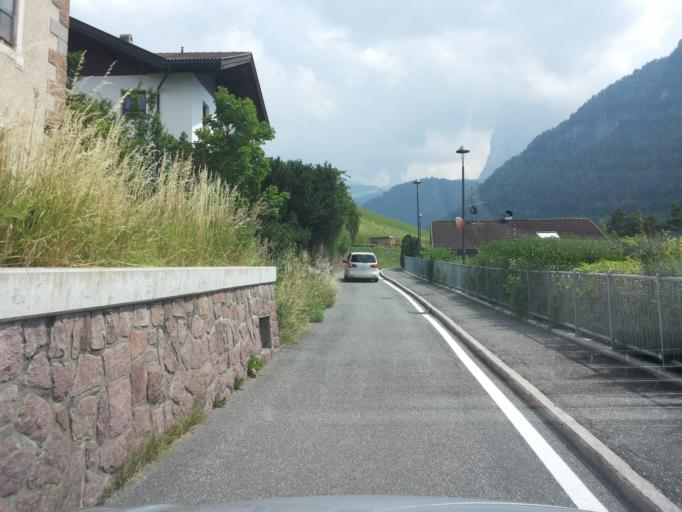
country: IT
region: Trentino-Alto Adige
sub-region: Bolzano
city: Ortisei
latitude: 46.5698
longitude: 11.6848
